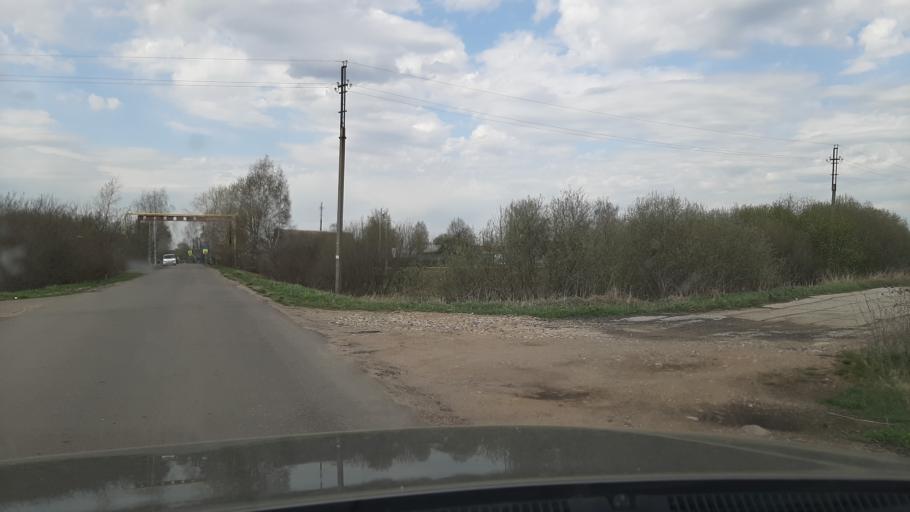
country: RU
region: Ivanovo
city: Privolzhsk
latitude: 57.3281
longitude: 41.2360
